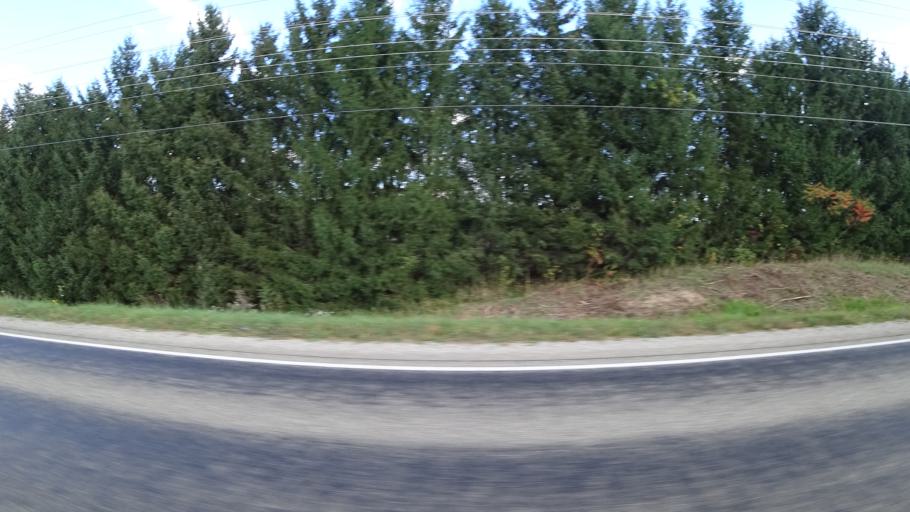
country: US
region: Michigan
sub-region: Saint Joseph County
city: Sturgis
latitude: 41.8244
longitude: -85.4285
